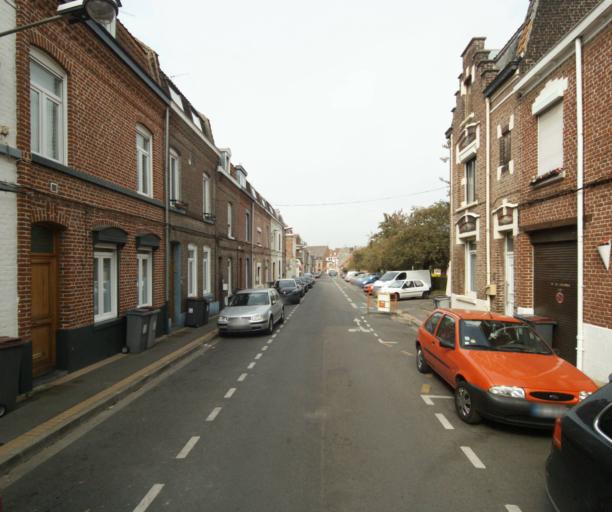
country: FR
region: Nord-Pas-de-Calais
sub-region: Departement du Nord
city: Haubourdin
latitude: 50.6096
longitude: 2.9944
